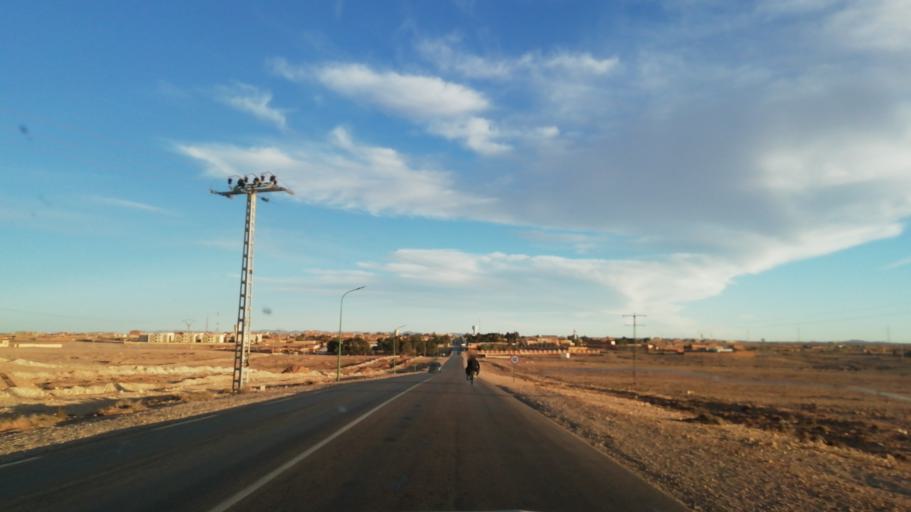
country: DZ
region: Wilaya de Naama
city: Naama
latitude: 33.7233
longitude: -0.7385
